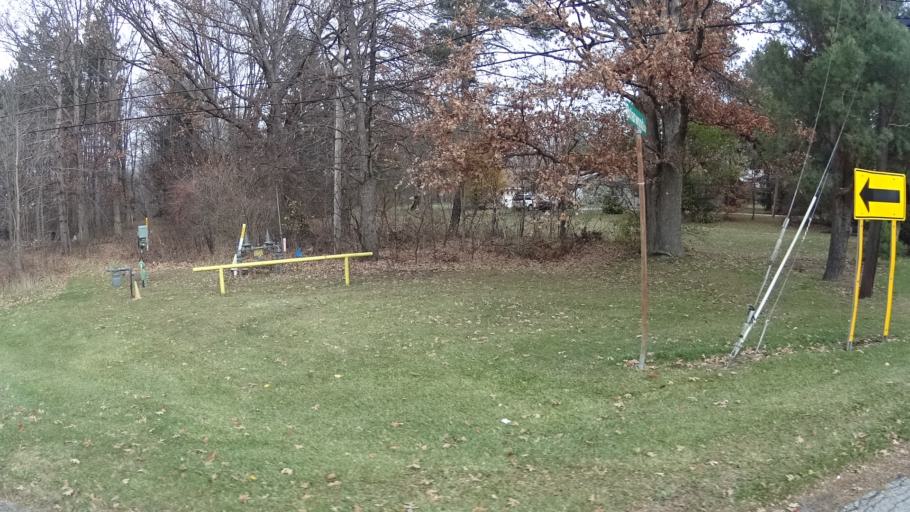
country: US
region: Ohio
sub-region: Cuyahoga County
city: Olmsted Falls
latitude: 41.3015
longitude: -81.9256
